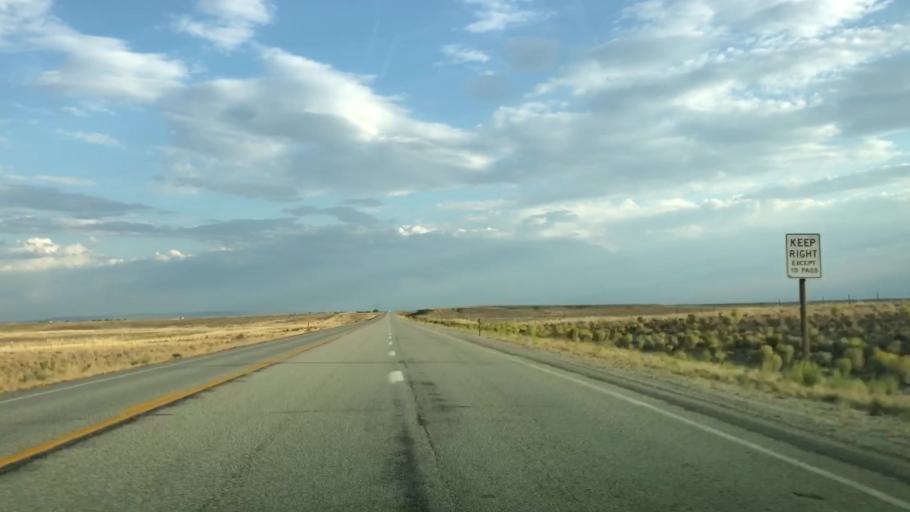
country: US
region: Wyoming
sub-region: Sweetwater County
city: North Rock Springs
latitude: 42.1849
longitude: -109.4787
